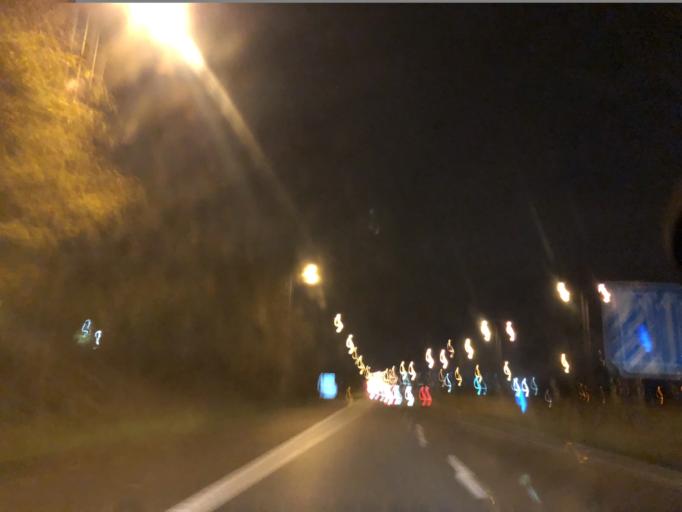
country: GB
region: England
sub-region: Kirklees
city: Cleckheaton
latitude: 53.7394
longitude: -1.7290
